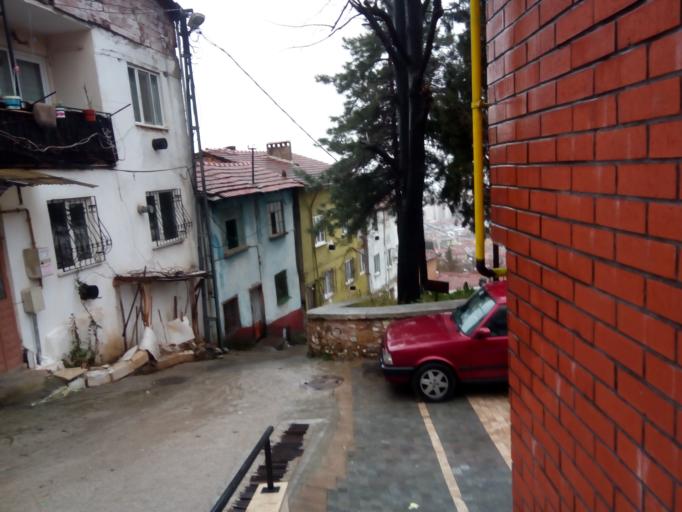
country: TR
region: Bursa
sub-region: Osmangazi
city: Bursa
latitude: 40.1769
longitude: 29.0588
